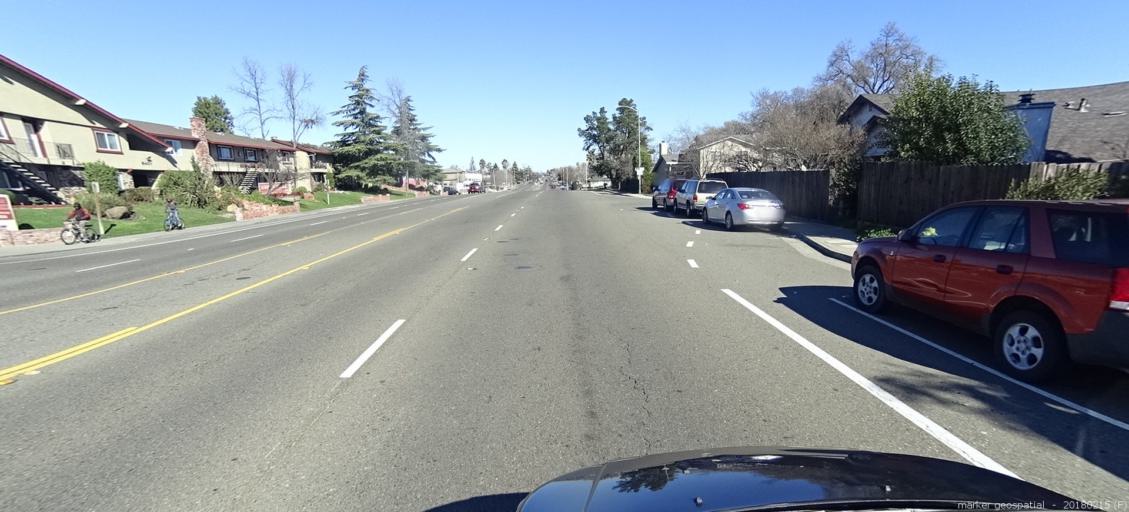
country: US
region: California
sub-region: Sacramento County
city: Foothill Farms
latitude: 38.6643
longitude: -121.3367
